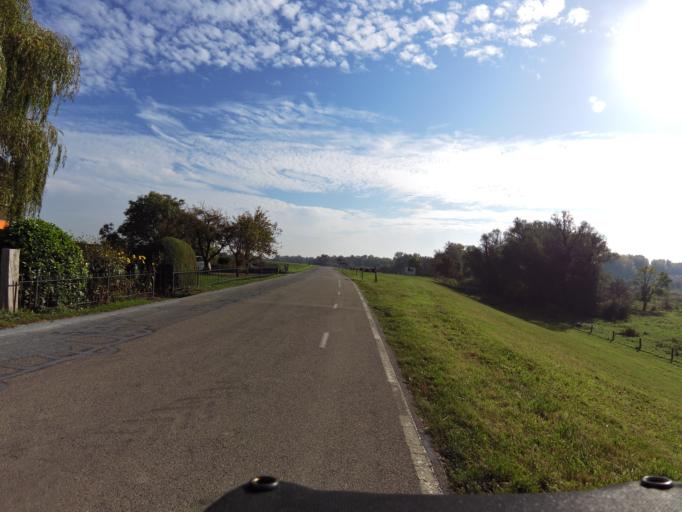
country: NL
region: Utrecht
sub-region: Gemeente Rhenen
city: Rhenen
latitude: 51.9490
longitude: 5.6180
